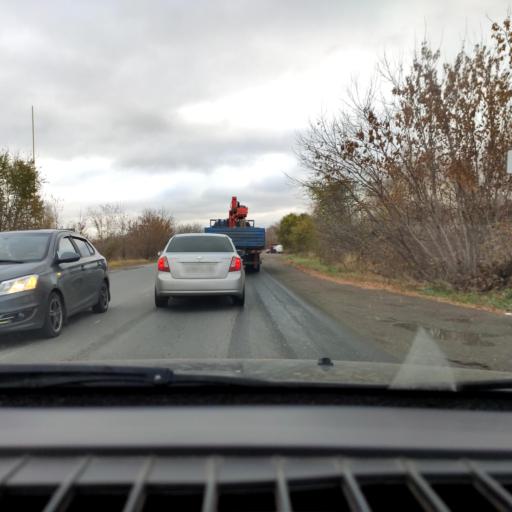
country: RU
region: Samara
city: Tol'yatti
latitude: 53.5600
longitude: 49.3589
